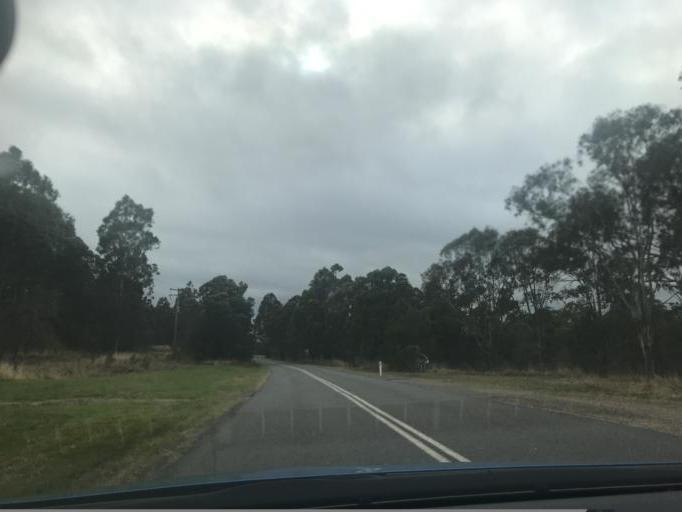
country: AU
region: New South Wales
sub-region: Cessnock
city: Cessnock
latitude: -32.7904
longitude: 151.2889
